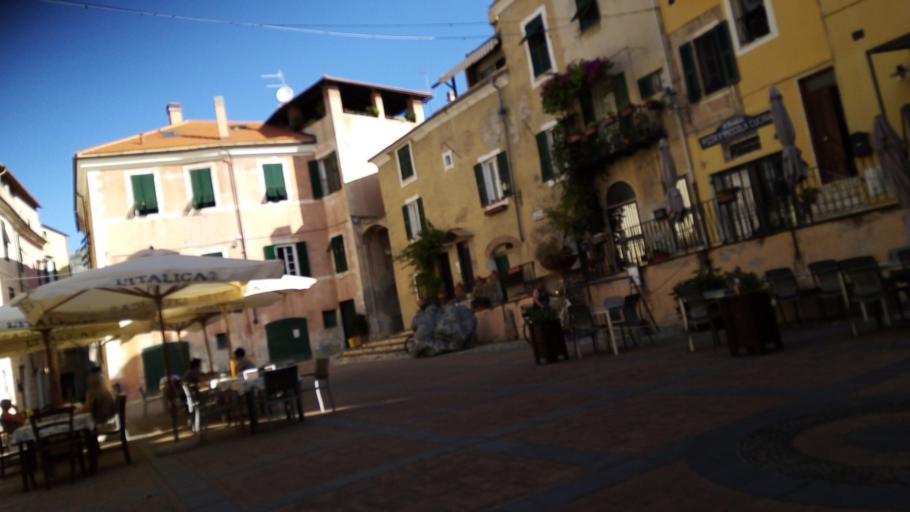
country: IT
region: Liguria
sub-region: Provincia di Savona
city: Toirano
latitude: 44.1259
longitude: 8.2096
